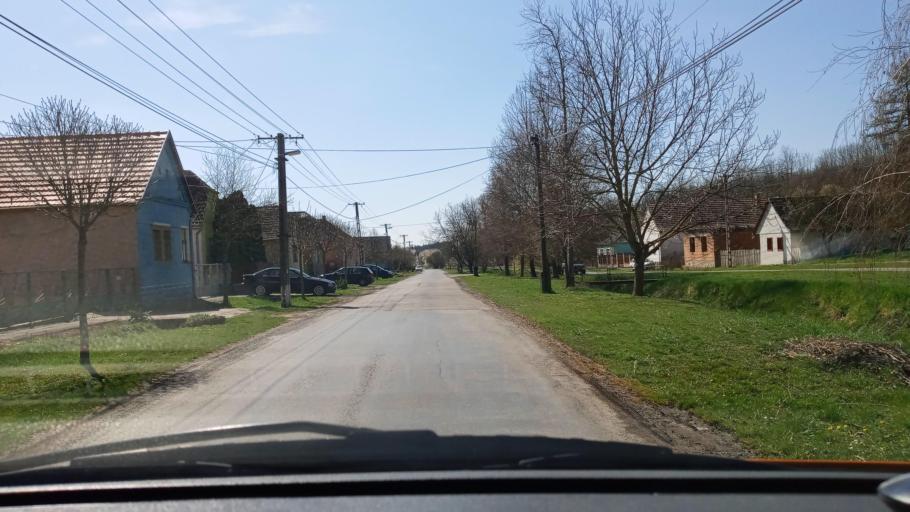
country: HU
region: Baranya
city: Pecsvarad
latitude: 46.0664
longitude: 18.4493
